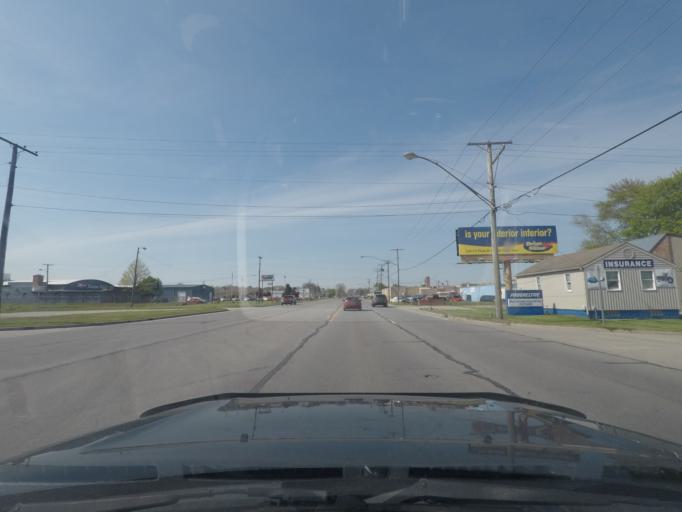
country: US
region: Indiana
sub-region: Elkhart County
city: Elkhart
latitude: 41.6969
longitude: -86.0036
